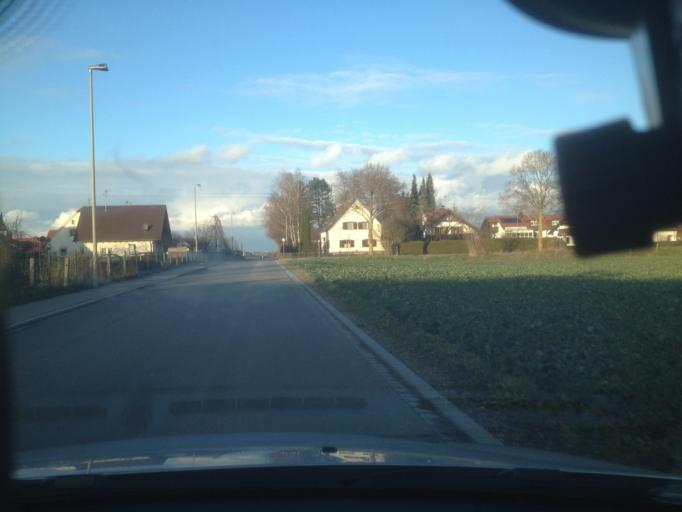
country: DE
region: Bavaria
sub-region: Upper Bavaria
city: Prittriching
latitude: 48.2042
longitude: 10.9319
